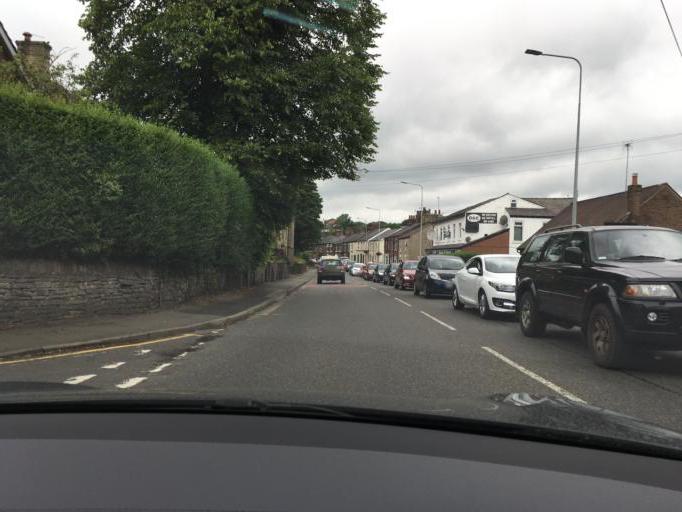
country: GB
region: England
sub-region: Cheshire East
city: Disley
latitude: 53.3600
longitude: -2.0334
